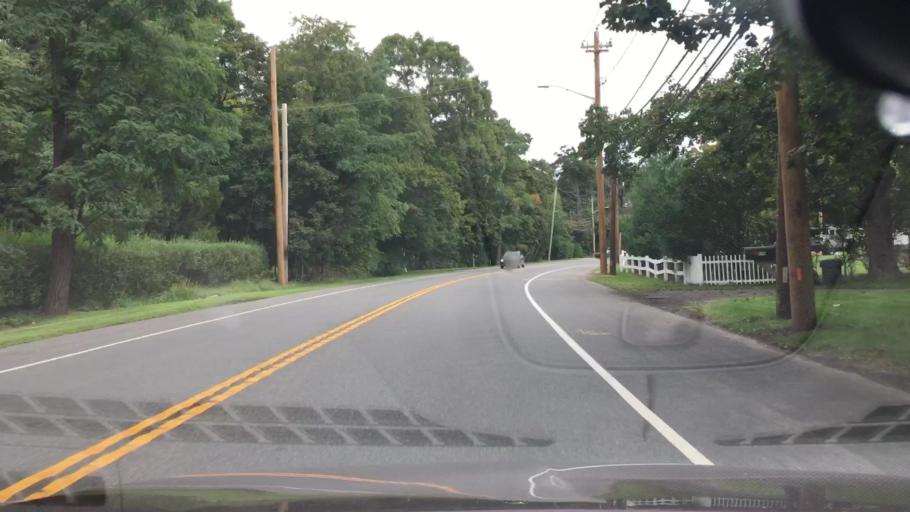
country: US
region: New York
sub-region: Suffolk County
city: Saint James
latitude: 40.8831
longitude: -73.1659
